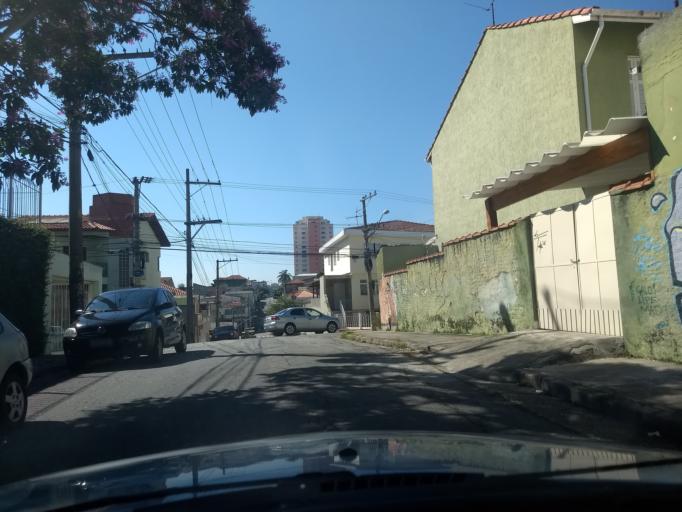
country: BR
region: Sao Paulo
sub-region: Sao Paulo
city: Sao Paulo
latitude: -23.4931
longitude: -46.5990
